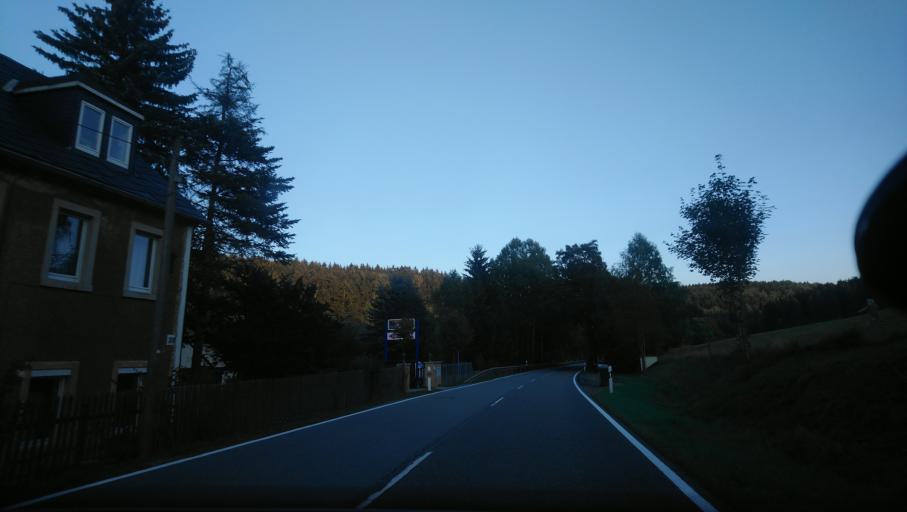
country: DE
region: Saxony
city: Tannenberg
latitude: 50.6069
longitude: 12.9747
